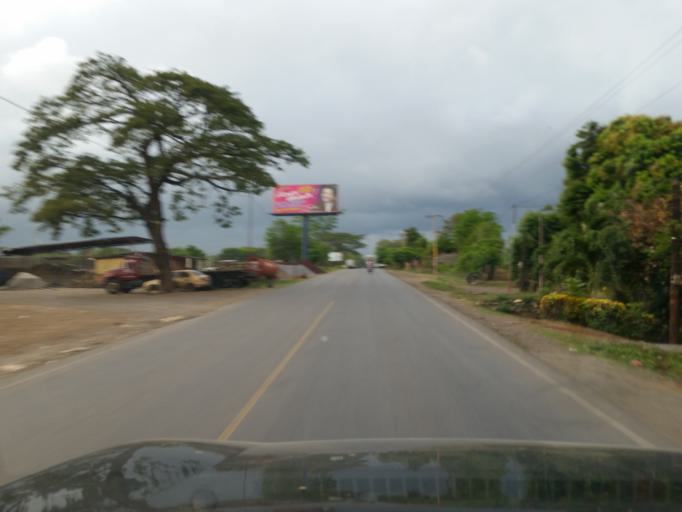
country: NI
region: Granada
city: Nandaime
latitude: 11.7613
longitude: -86.0476
